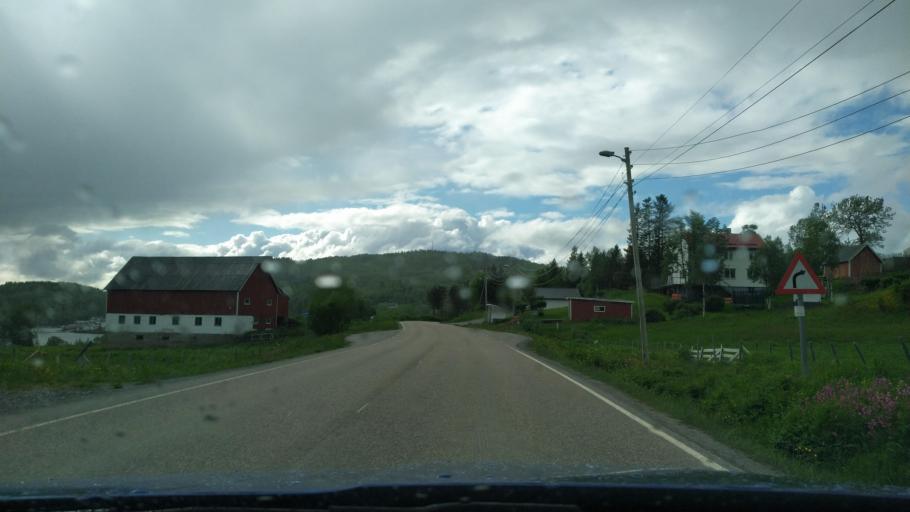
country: NO
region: Troms
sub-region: Sorreisa
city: Sorreisa
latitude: 69.1613
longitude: 18.1216
